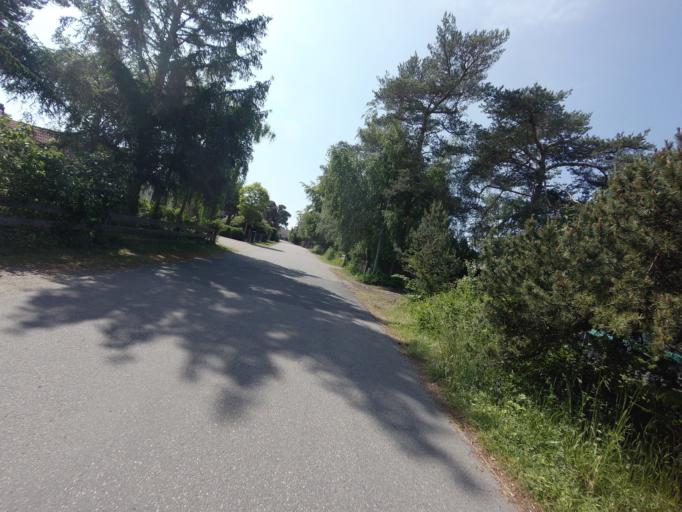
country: SE
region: Skane
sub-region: Vellinge Kommun
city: Hollviken
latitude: 55.4040
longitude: 12.9766
